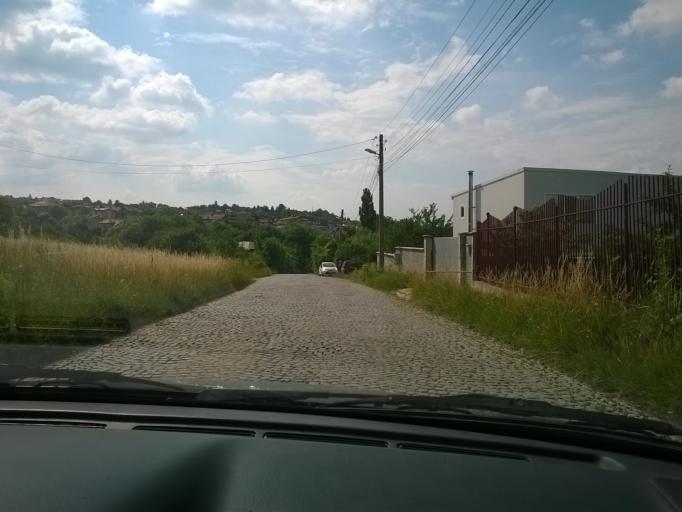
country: BG
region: Sofiya
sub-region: Obshtina Bozhurishte
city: Bozhurishte
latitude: 42.6822
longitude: 23.2390
